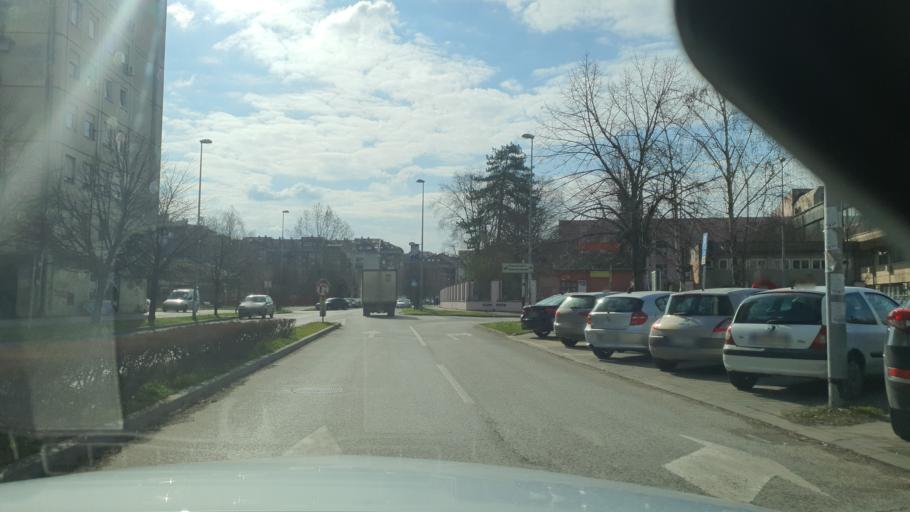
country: RS
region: Autonomna Pokrajina Vojvodina
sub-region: Juznobacki Okrug
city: Novi Sad
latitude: 45.2592
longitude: 19.8301
